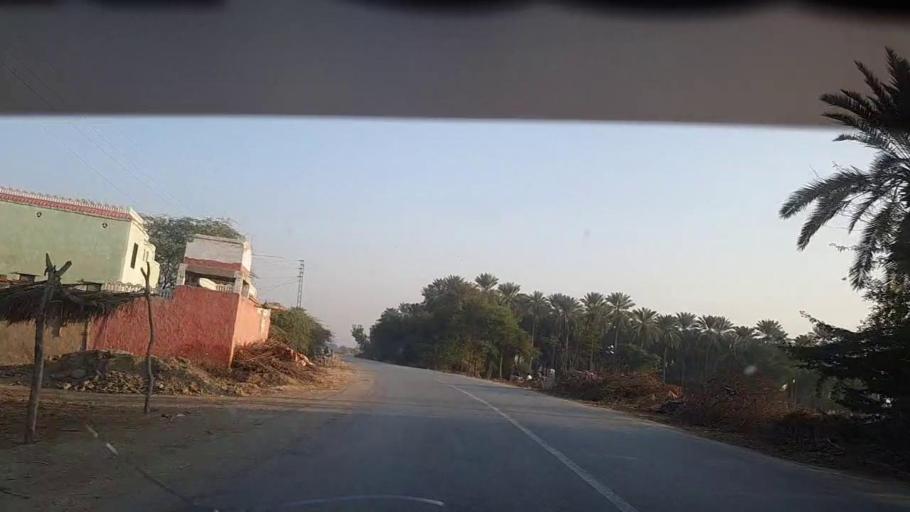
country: PK
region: Sindh
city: Ranipur
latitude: 27.2610
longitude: 68.5256
